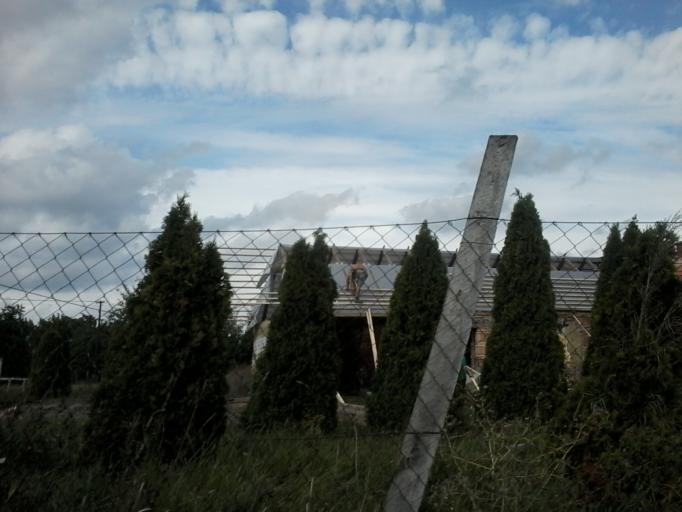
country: HU
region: Vas
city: Janoshaza
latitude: 47.0532
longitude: 17.1374
